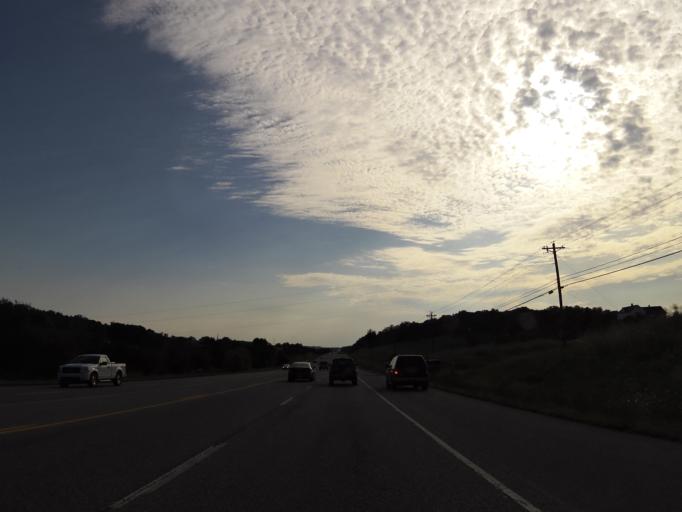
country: US
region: Tennessee
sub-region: Loudon County
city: Greenback
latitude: 35.6857
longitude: -84.0610
